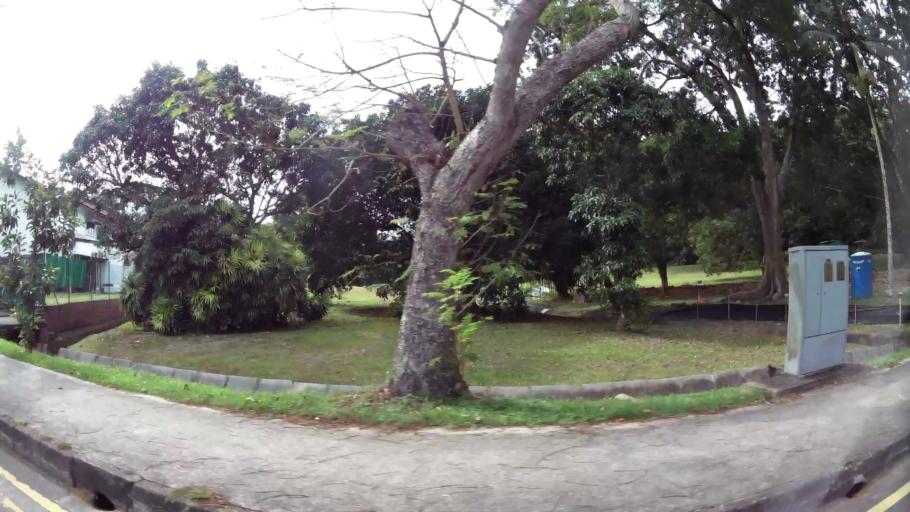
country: SG
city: Singapore
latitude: 1.3214
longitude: 103.7902
